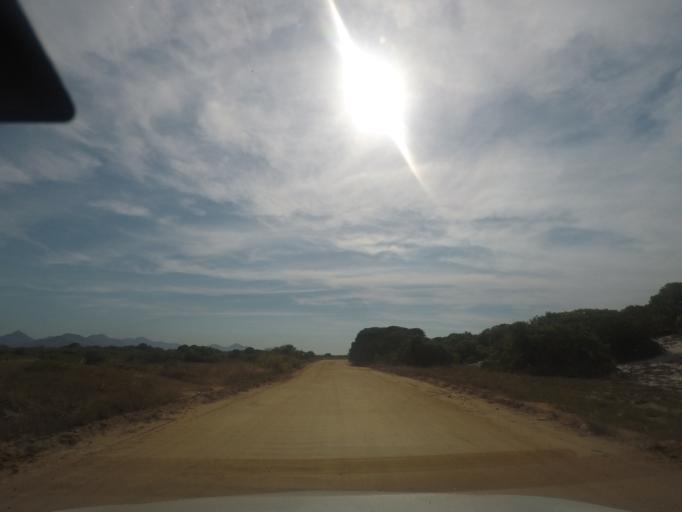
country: BR
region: Rio de Janeiro
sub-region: Marica
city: Marica
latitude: -22.9600
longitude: -42.8649
